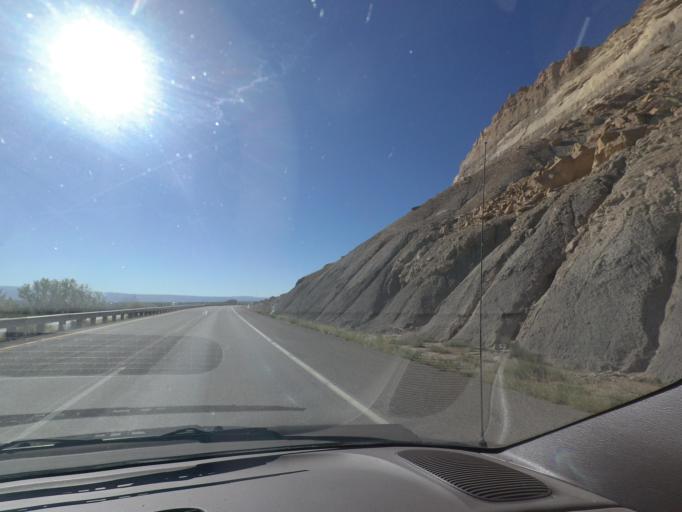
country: US
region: Colorado
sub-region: Mesa County
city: Palisade
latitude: 39.1176
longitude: -108.3483
